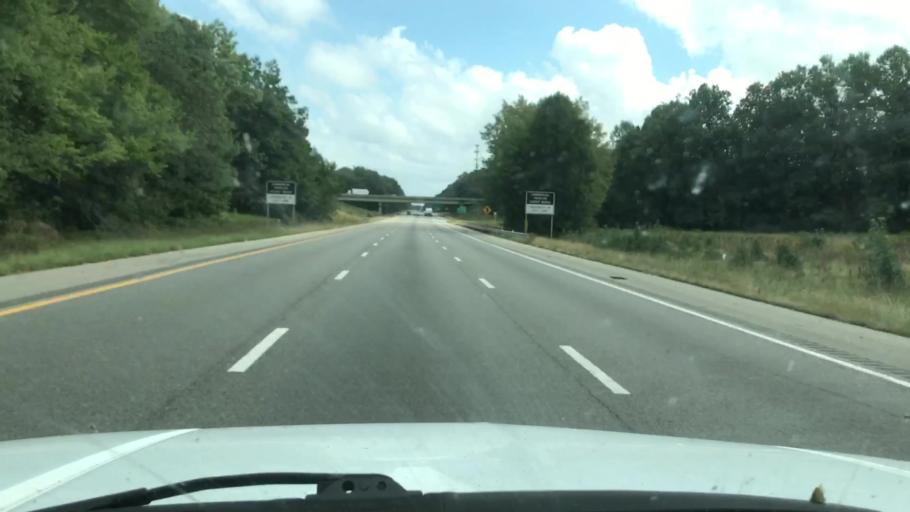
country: US
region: Virginia
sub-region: Henrico County
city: Short Pump
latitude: 37.6691
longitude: -77.5851
